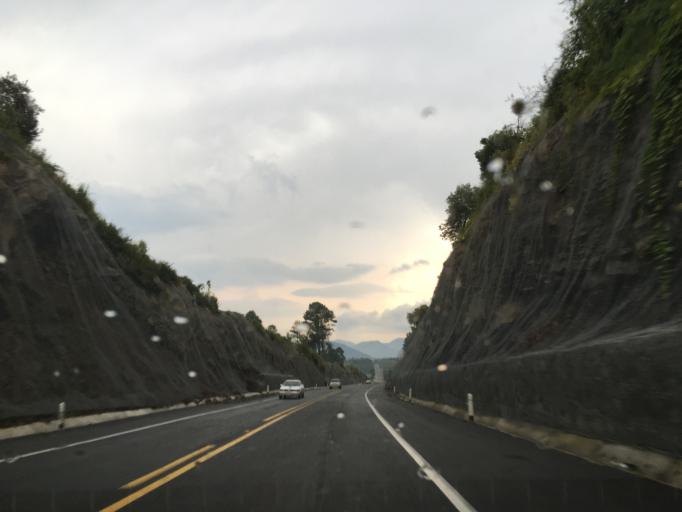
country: MX
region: Michoacan
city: Angahuan
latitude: 19.5084
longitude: -102.1569
